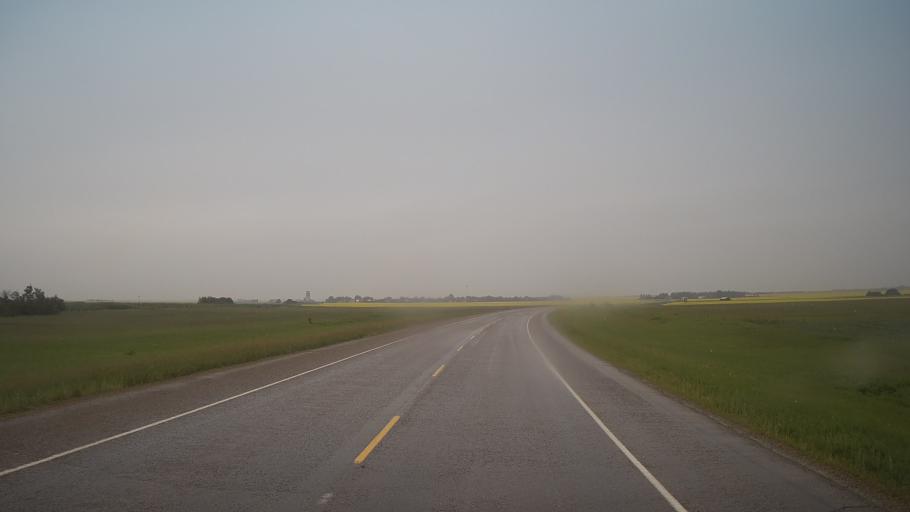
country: CA
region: Saskatchewan
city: Wilkie
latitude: 52.1912
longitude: -108.4216
